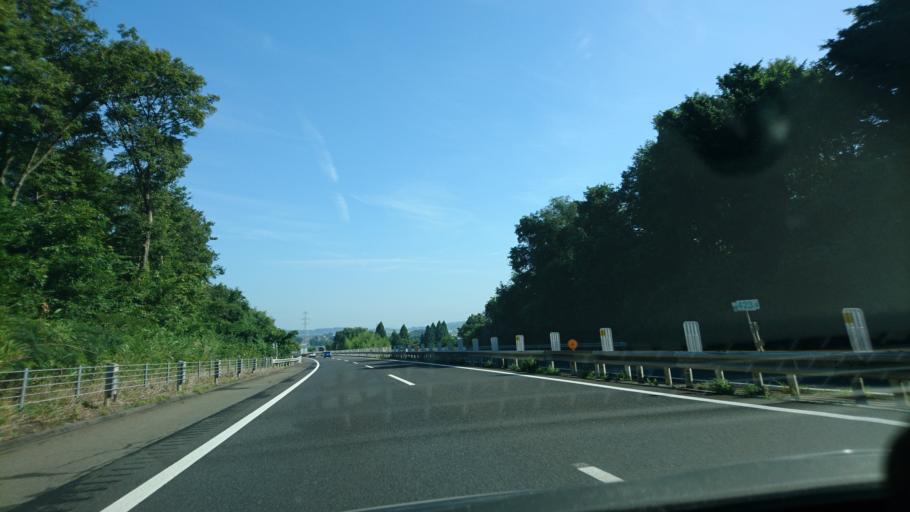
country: JP
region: Iwate
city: Ichinoseki
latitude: 38.9654
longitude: 141.1123
